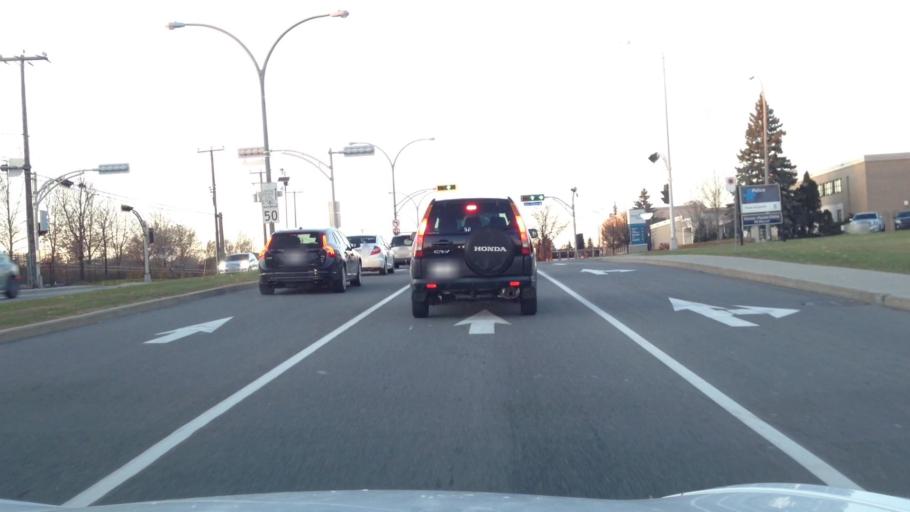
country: CA
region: Quebec
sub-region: Montreal
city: Pointe-Claire
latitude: 45.4469
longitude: -73.8168
